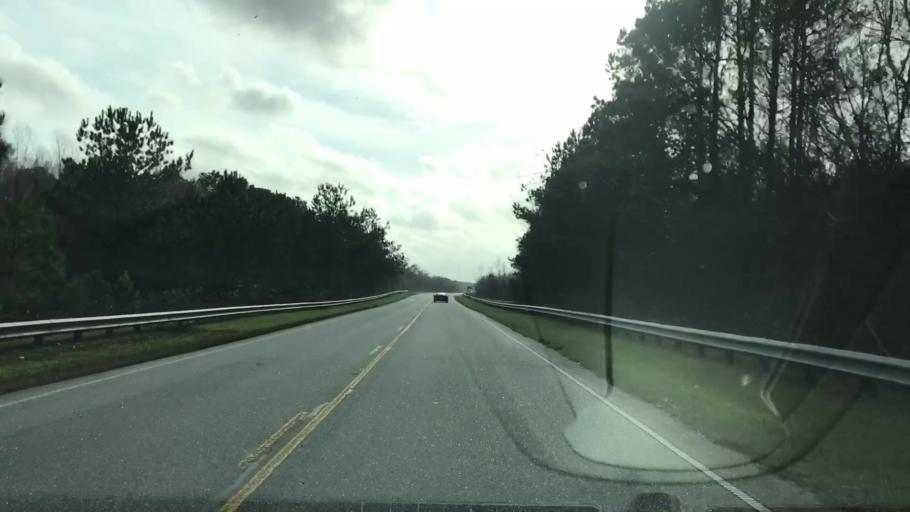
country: US
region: South Carolina
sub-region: Williamsburg County
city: Andrews
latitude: 33.3124
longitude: -79.6718
